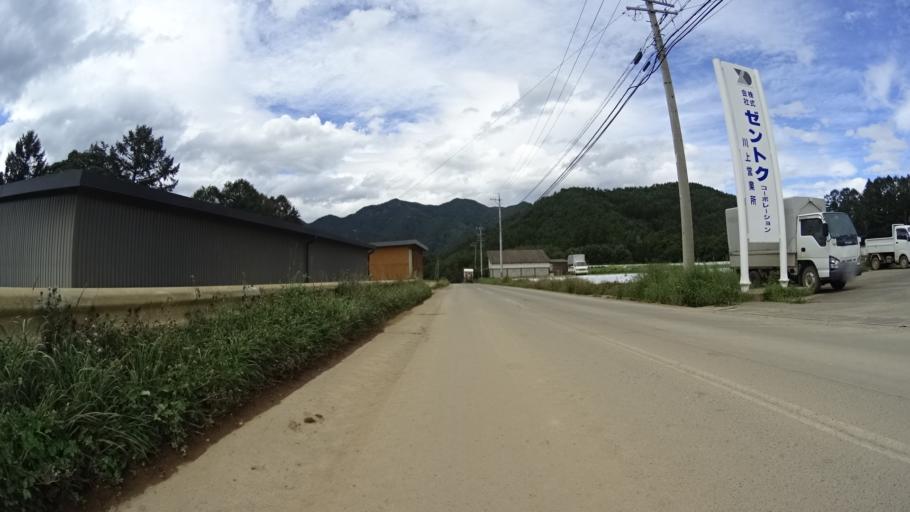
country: JP
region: Nagano
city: Saku
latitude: 35.9581
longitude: 138.5473
